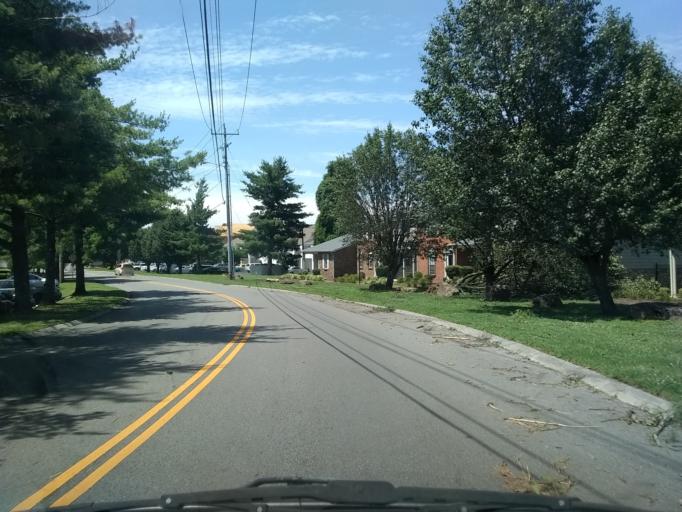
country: US
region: Tennessee
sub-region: Davidson County
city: Nashville
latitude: 36.1311
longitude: -86.7001
